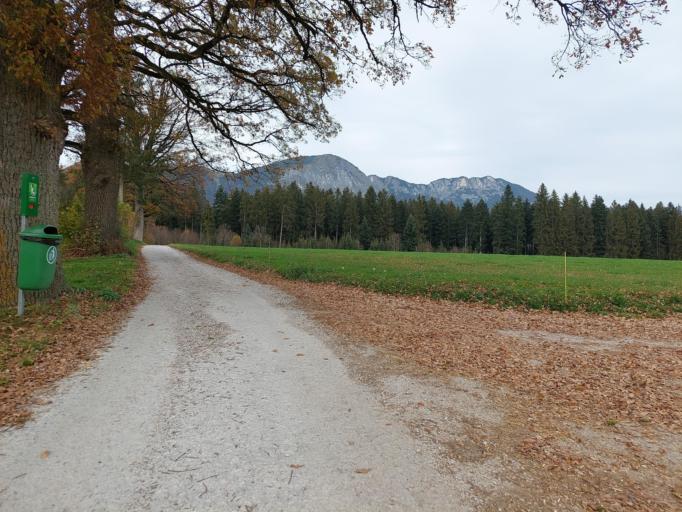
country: AT
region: Tyrol
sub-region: Politischer Bezirk Kufstein
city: Angath
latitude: 47.5022
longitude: 12.0429
